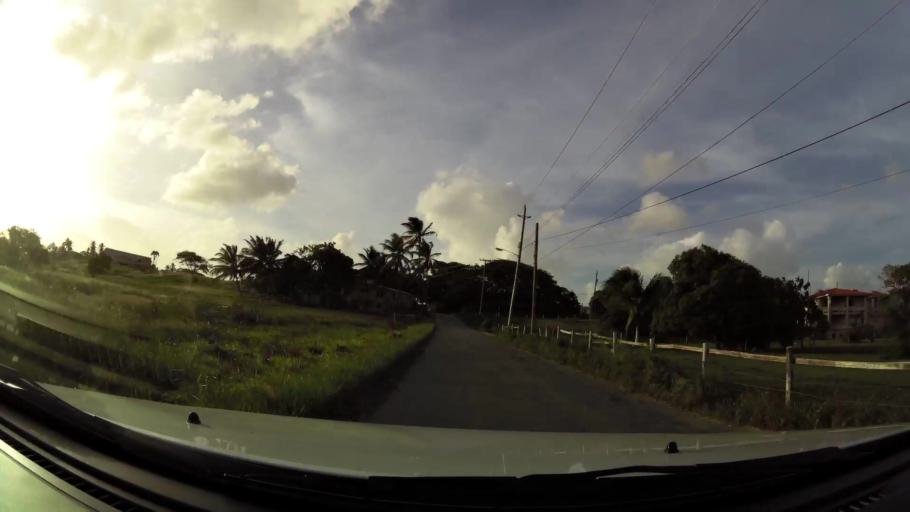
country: BB
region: Christ Church
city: Oistins
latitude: 13.0750
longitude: -59.5118
